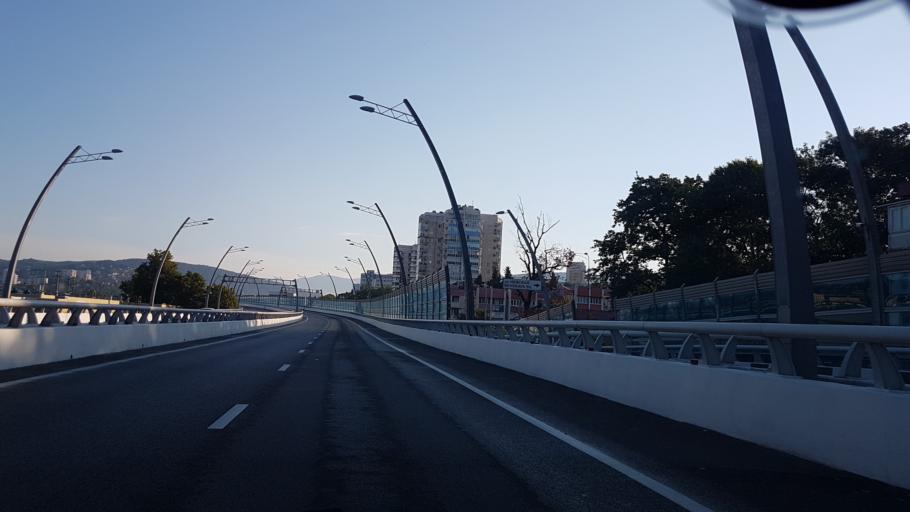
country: RU
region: Krasnodarskiy
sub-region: Sochi City
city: Sochi
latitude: 43.5935
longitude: 39.7311
